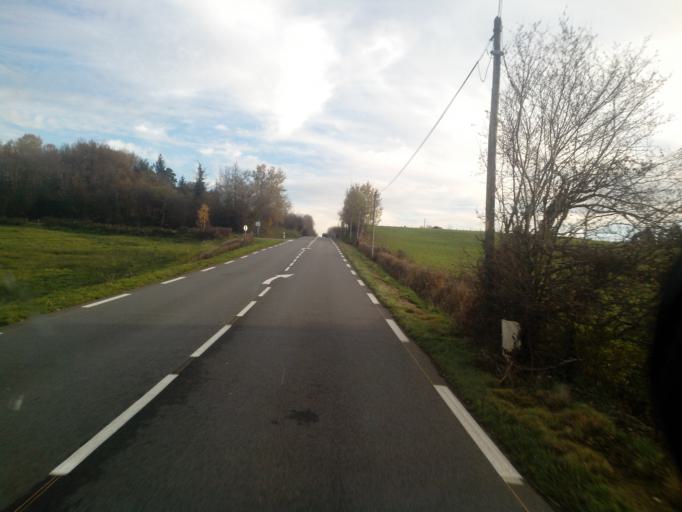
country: FR
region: Limousin
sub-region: Departement de la Haute-Vienne
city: Neuvic-Entier
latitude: 45.7445
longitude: 1.6037
